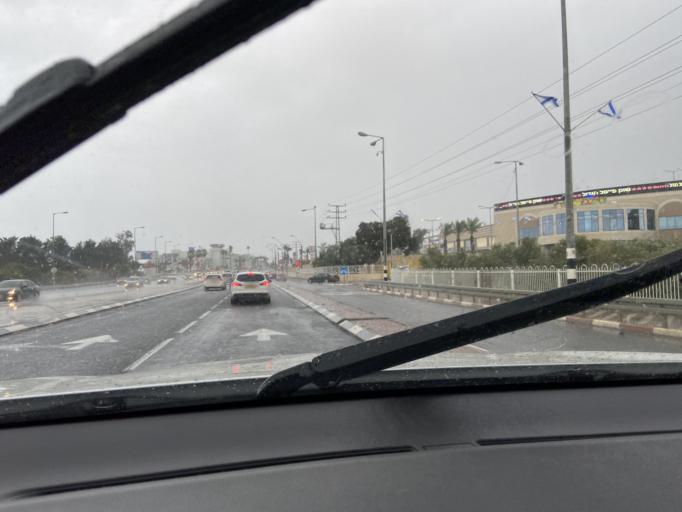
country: IL
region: Northern District
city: El Mazra`a
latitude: 32.9859
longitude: 35.0952
